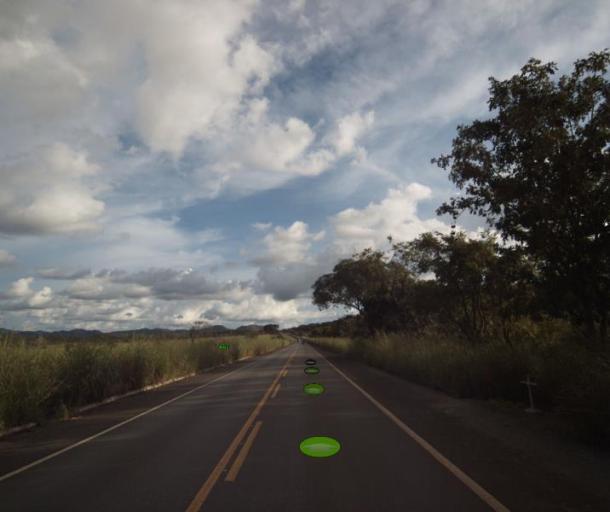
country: BR
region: Goias
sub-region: Niquelandia
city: Niquelandia
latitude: -14.5430
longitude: -48.5513
